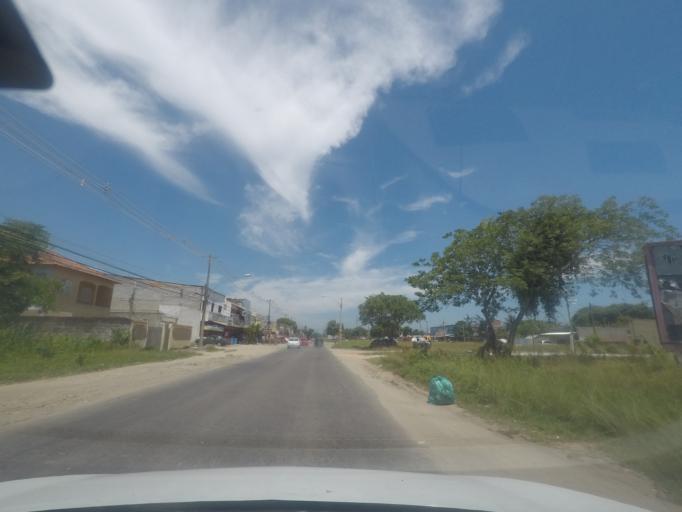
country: BR
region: Rio de Janeiro
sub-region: Itaguai
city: Itaguai
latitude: -22.9791
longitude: -43.6689
